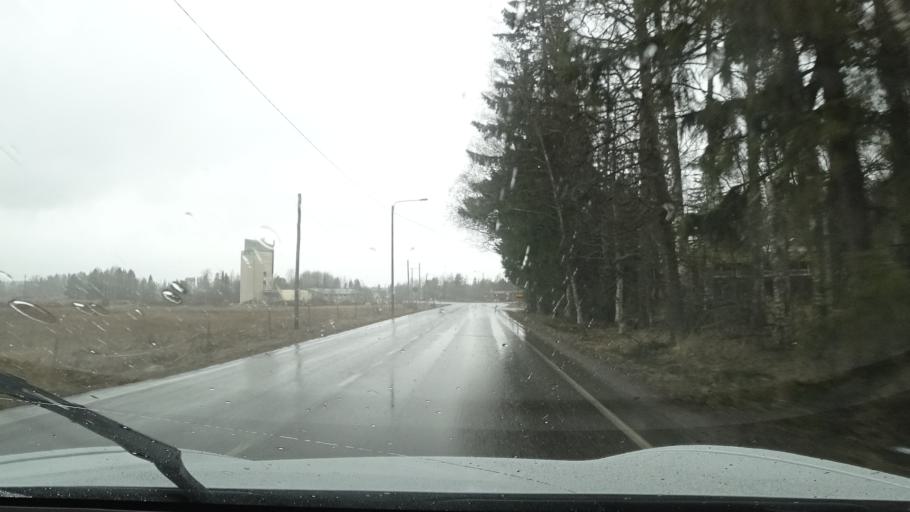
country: FI
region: Paijanne Tavastia
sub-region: Lahti
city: Orimattila
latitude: 60.8011
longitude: 25.7714
